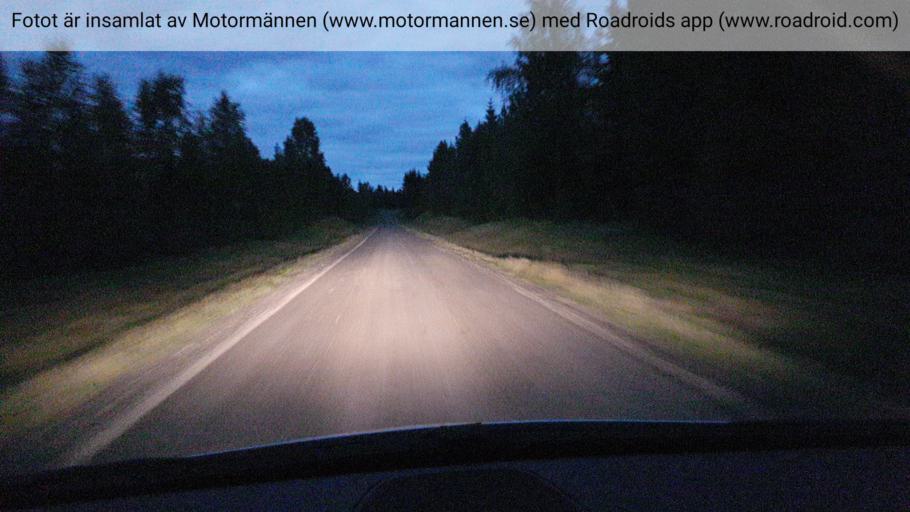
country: SE
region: Jaemtland
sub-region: Braecke Kommun
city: Braecke
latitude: 63.2351
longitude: 15.3606
